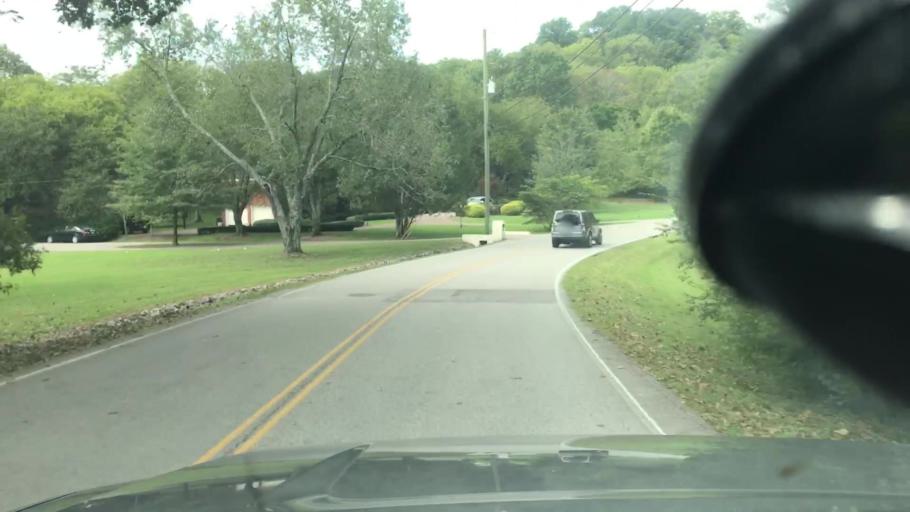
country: US
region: Tennessee
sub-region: Davidson County
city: Forest Hills
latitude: 36.0597
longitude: -86.8538
